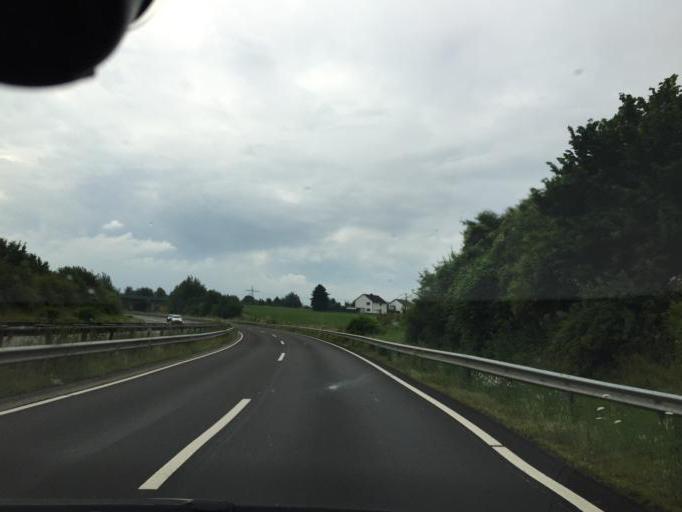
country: DE
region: Rheinland-Pfalz
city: Melsbach
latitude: 50.4778
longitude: 7.4900
